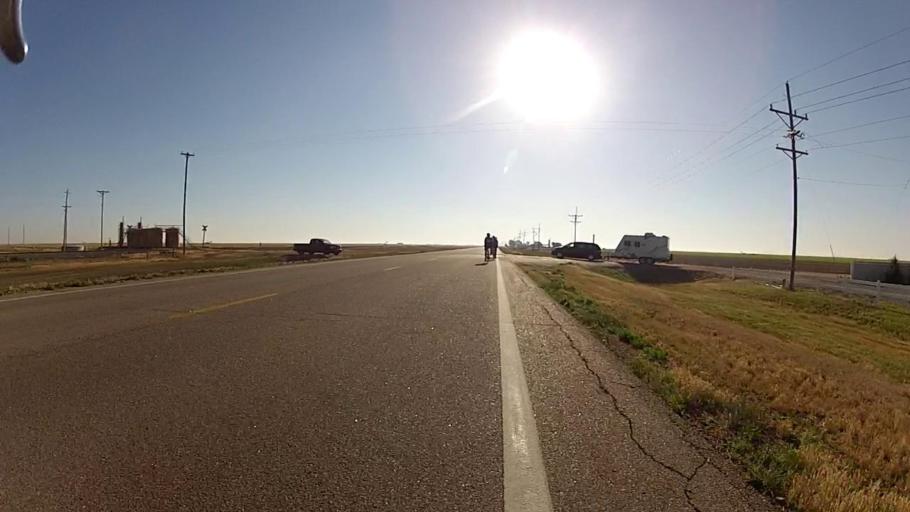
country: US
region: Kansas
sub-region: Haskell County
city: Sublette
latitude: 37.4959
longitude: -100.7988
